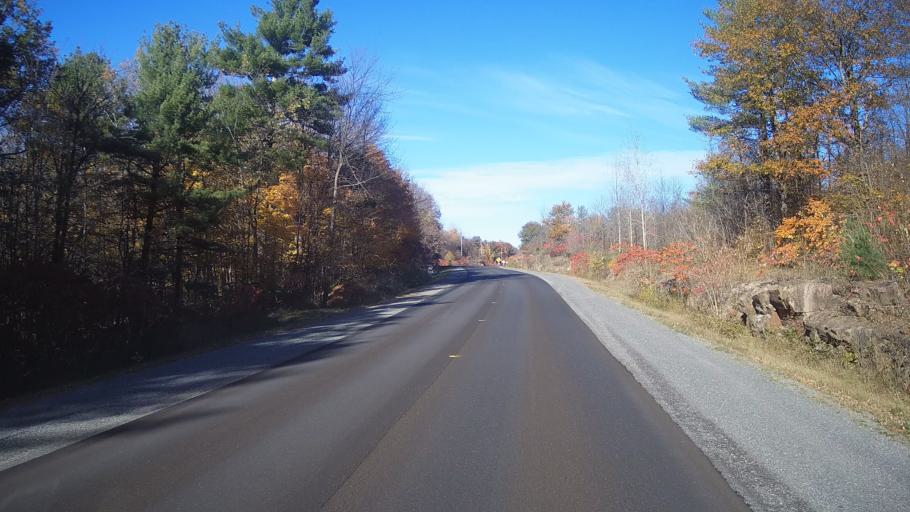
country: CA
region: Ontario
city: Kingston
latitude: 44.5059
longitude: -76.4729
